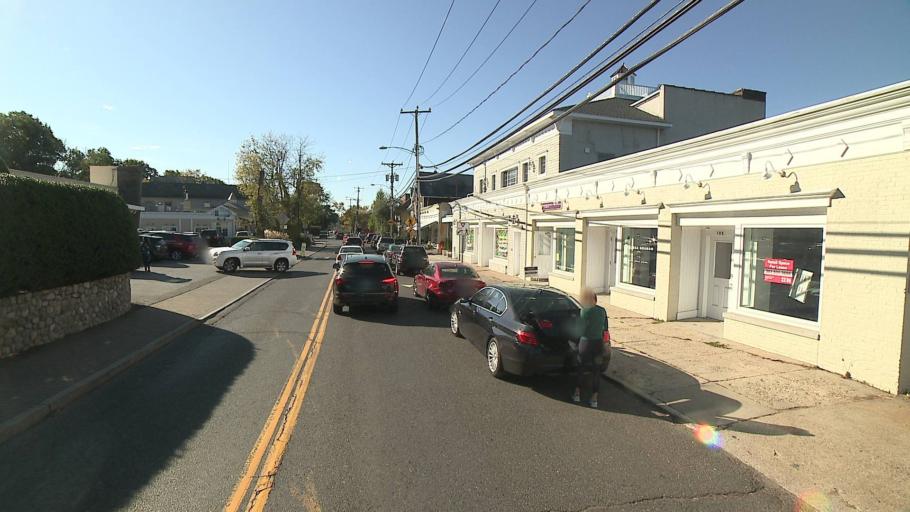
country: US
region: Connecticut
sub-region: Fairfield County
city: Darien
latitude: 41.0688
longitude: -73.4435
